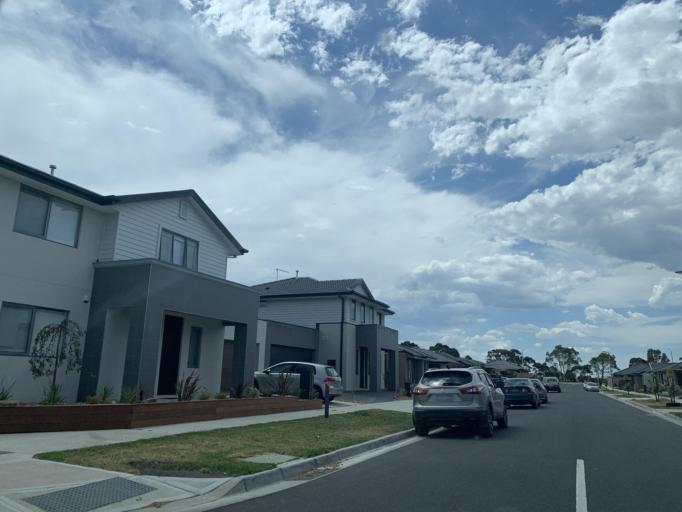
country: AU
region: Victoria
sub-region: Casey
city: Cranbourne South
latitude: -38.1249
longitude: 145.2426
